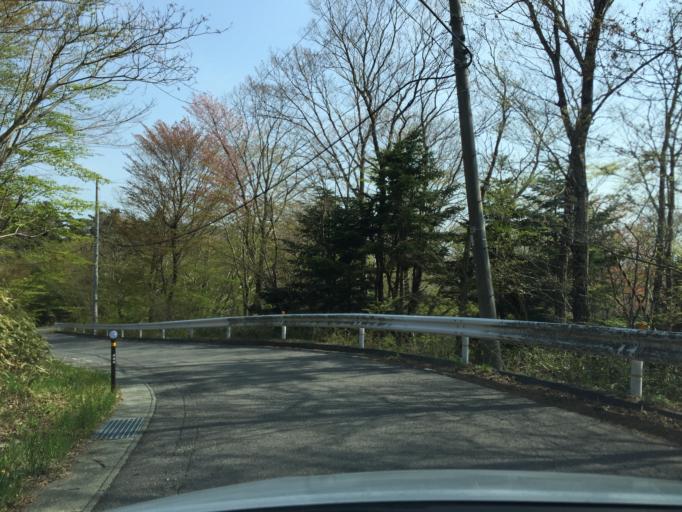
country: JP
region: Fukushima
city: Iwaki
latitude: 37.1992
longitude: 140.8501
